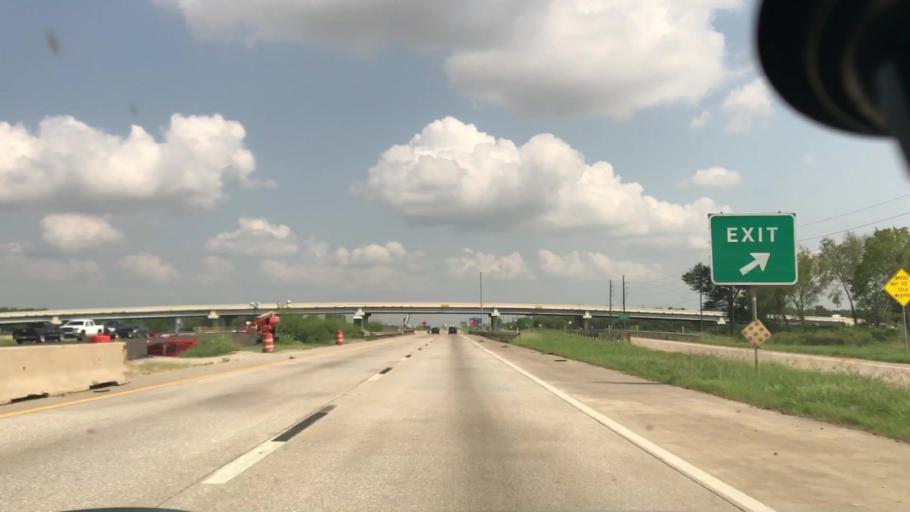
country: US
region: Texas
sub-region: Brazoria County
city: Iowa Colony
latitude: 29.5236
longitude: -95.3865
